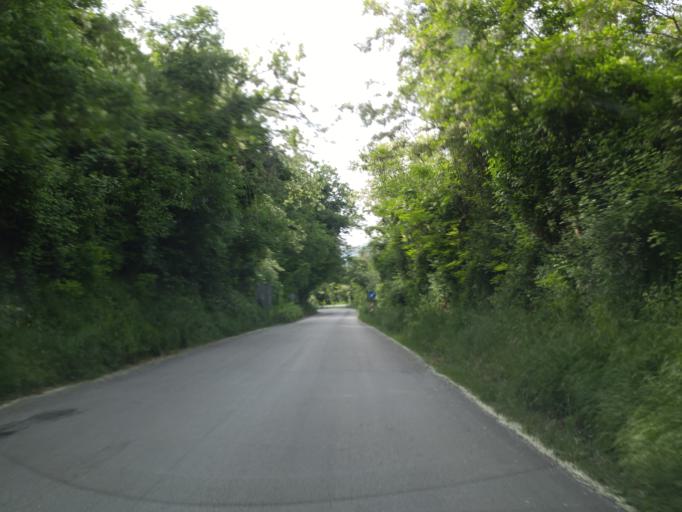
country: IT
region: The Marches
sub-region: Provincia di Pesaro e Urbino
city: Canavaccio
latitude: 43.6678
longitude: 12.7538
